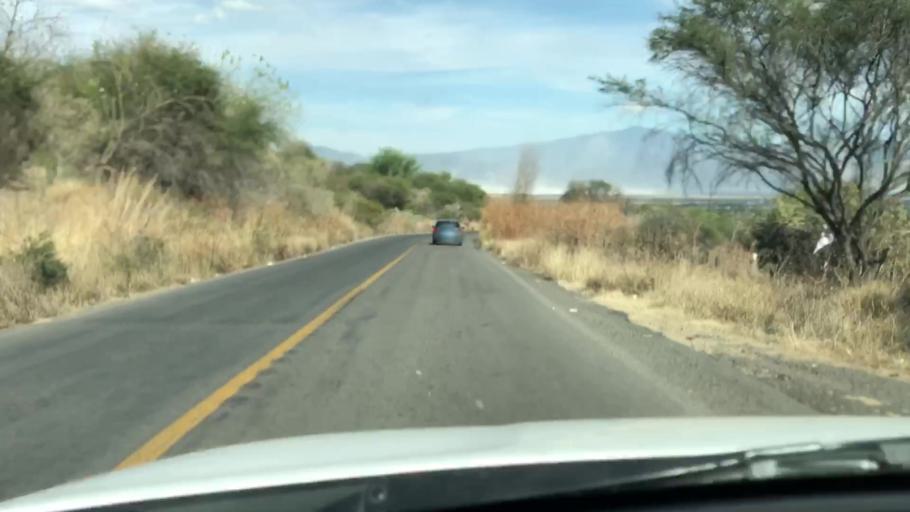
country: MX
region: Jalisco
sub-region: Zacoalco de Torres
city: Barranca de Otates (Barranca de Otatan)
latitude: 20.2602
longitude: -103.6518
